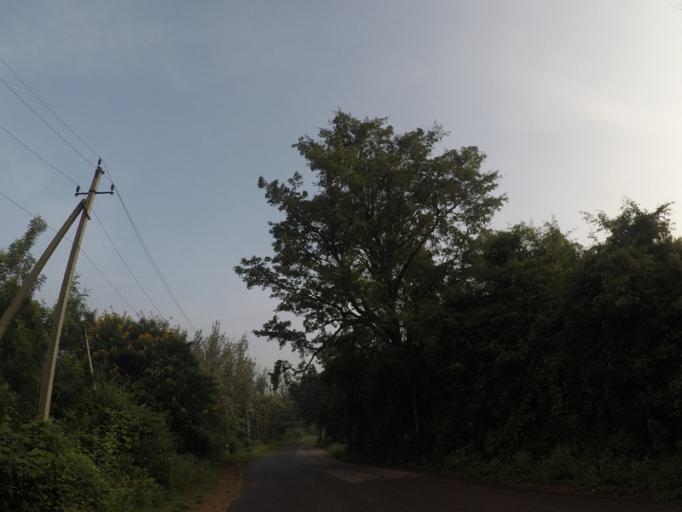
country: IN
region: Karnataka
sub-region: Chikmagalur
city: Chikmagalur
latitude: 13.3921
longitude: 75.7794
